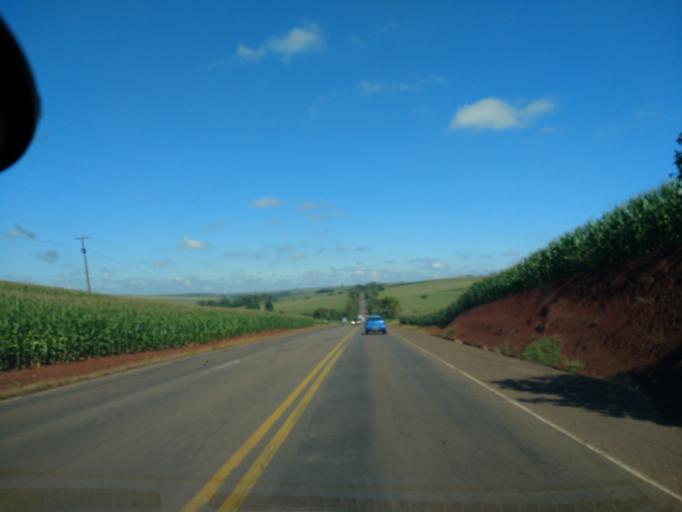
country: BR
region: Parana
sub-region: Terra Boa
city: Terra Boa
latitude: -23.6121
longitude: -52.4252
